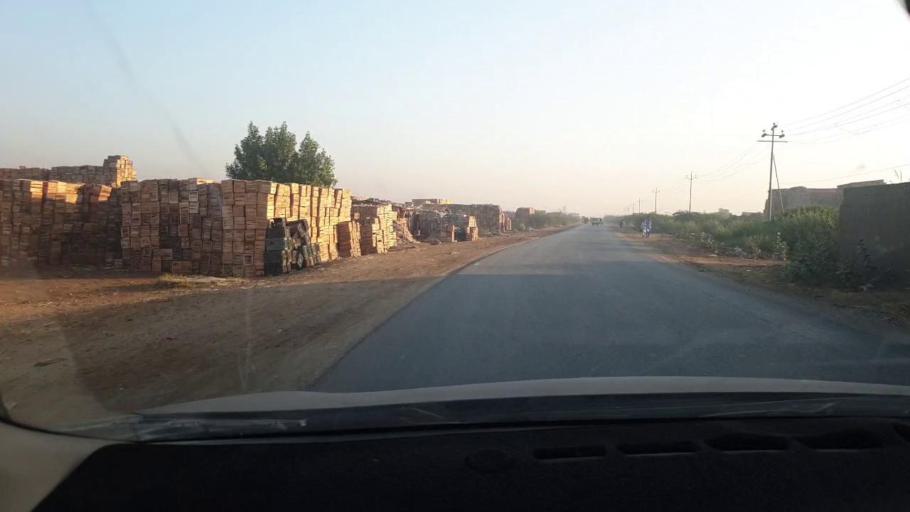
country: PK
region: Sindh
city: Malir Cantonment
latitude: 24.9974
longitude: 67.1437
